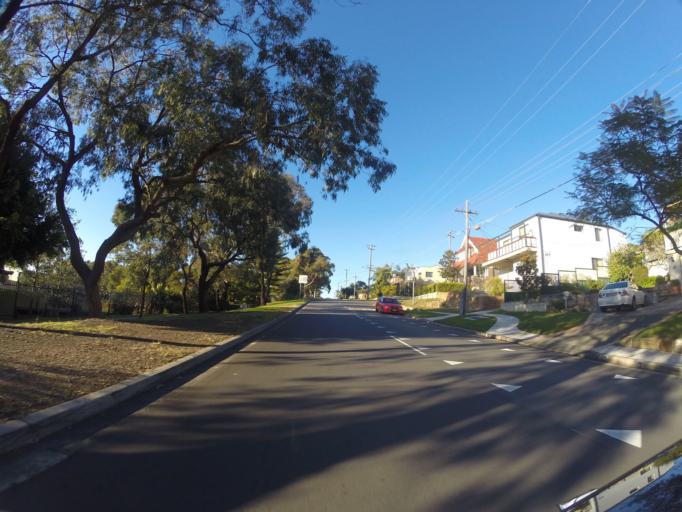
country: AU
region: New South Wales
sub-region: Sutherland Shire
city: Miranda
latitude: -34.0483
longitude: 151.1022
